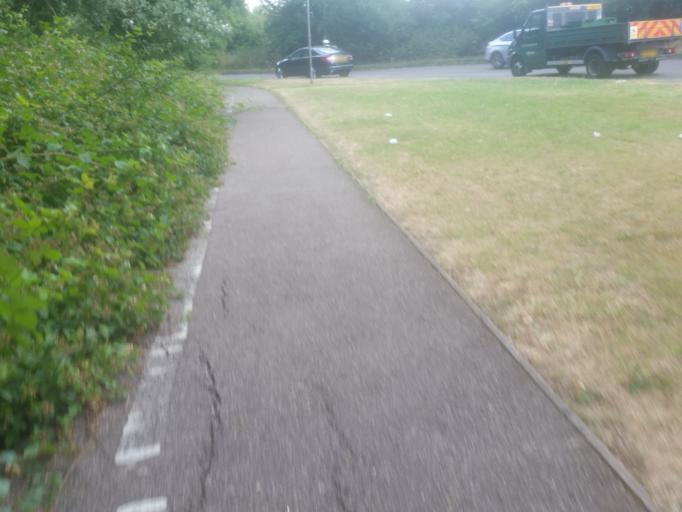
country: GB
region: England
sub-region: Hertfordshire
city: Borehamwood
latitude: 51.6447
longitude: -0.2603
